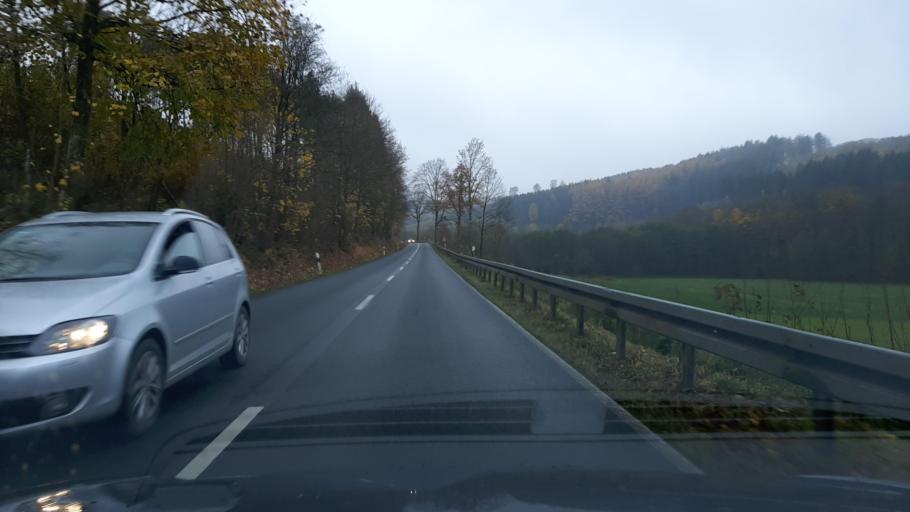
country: DE
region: North Rhine-Westphalia
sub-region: Regierungsbezirk Arnsberg
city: Olsberg
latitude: 51.2649
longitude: 8.4737
